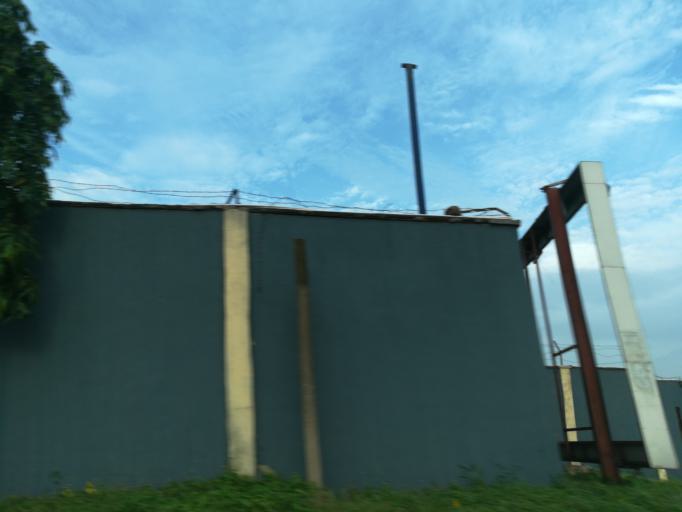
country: NG
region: Lagos
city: Oshodi
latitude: 6.5789
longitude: 3.3341
